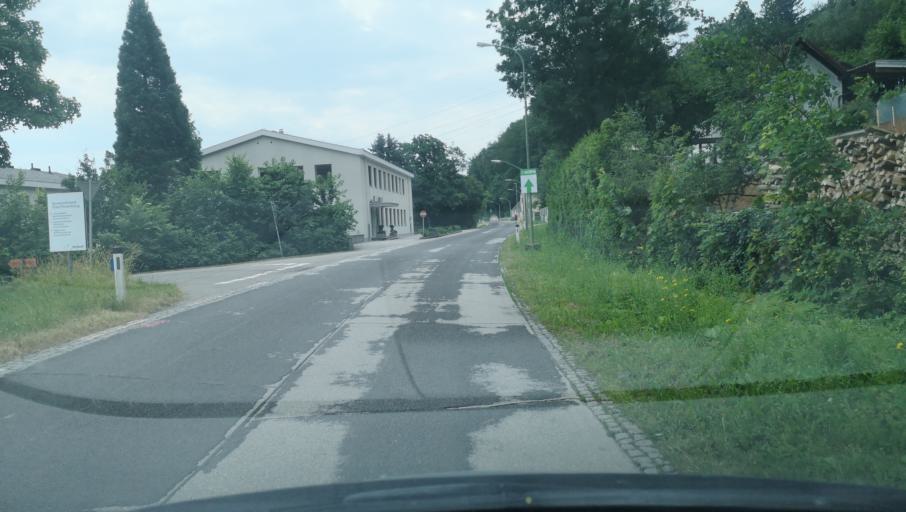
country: AT
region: Lower Austria
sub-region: Politischer Bezirk Melk
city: Ybbs an der Donau
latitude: 48.1895
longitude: 15.0633
